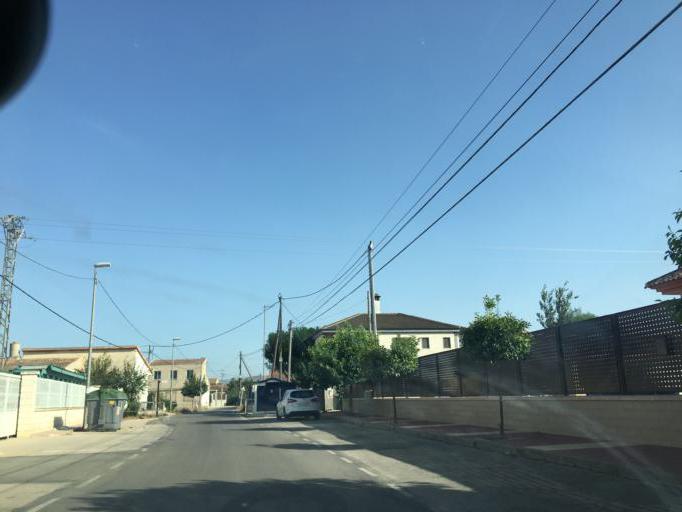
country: ES
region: Murcia
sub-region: Murcia
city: Santomera
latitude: 38.0275
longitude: -1.0655
